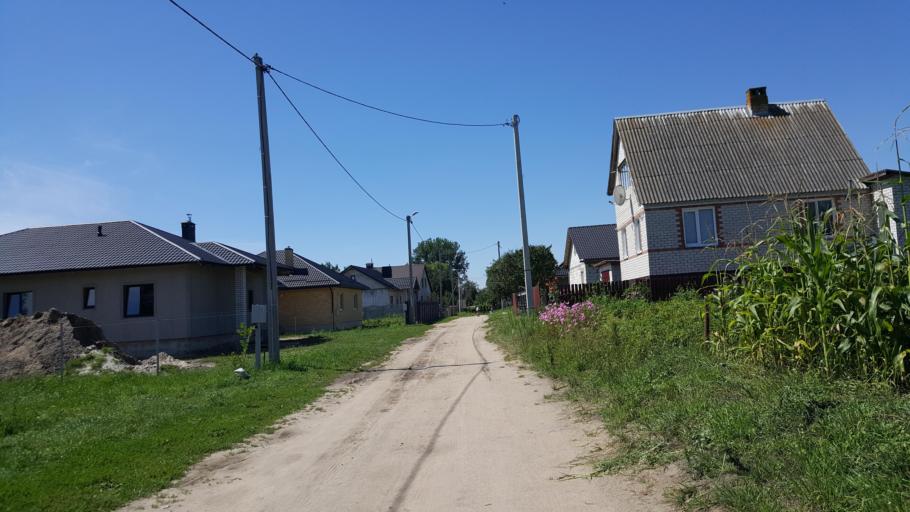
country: BY
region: Brest
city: Charnawchytsy
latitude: 52.2217
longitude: 23.7627
